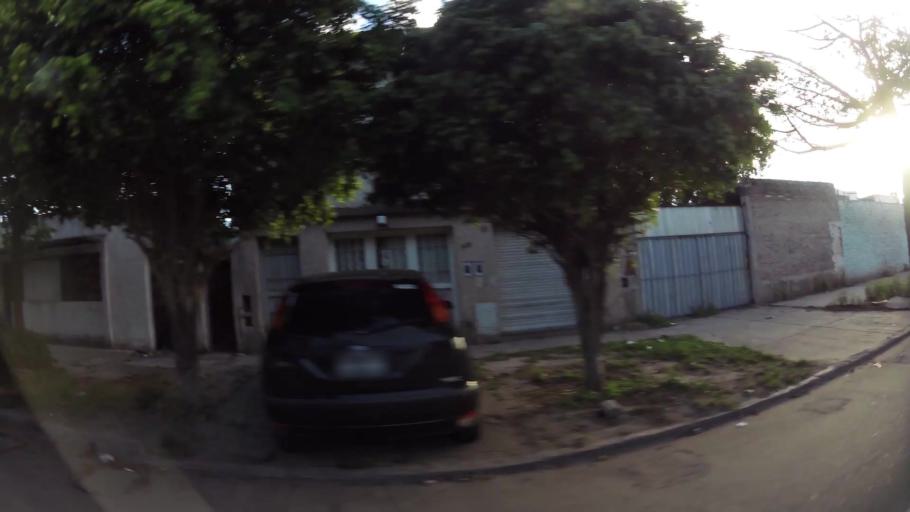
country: AR
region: Santa Fe
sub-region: Departamento de Rosario
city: Rosario
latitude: -32.9782
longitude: -60.6652
